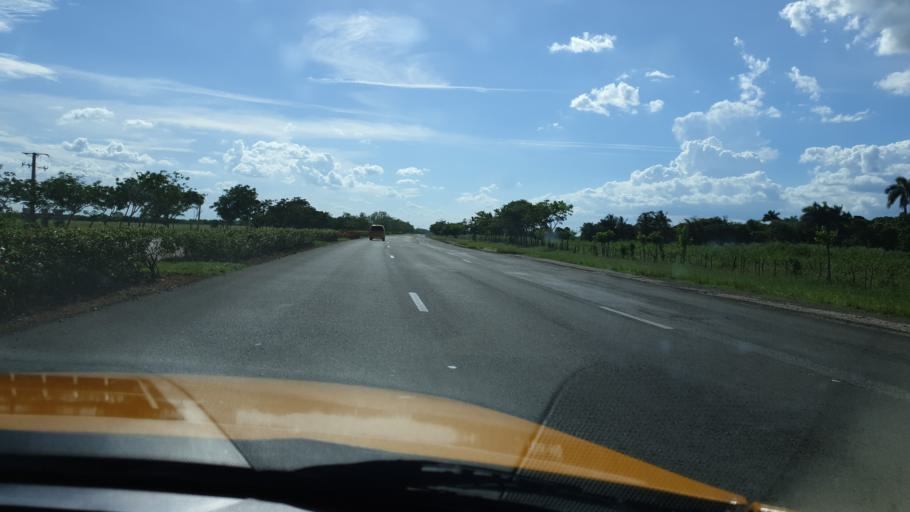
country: CU
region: Cienfuegos
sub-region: Municipio de Aguada de Pasajeros
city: Aguada de Pasajeros
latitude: 22.4098
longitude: -80.8899
